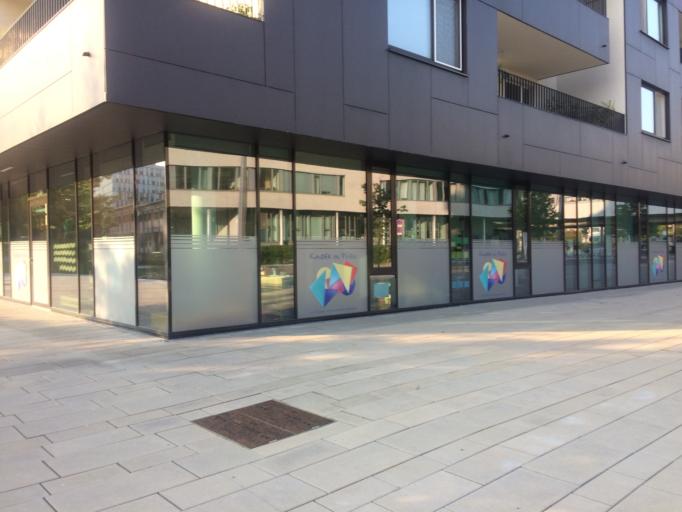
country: AT
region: Vienna
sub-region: Wien Stadt
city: Vienna
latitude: 48.2121
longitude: 16.4166
